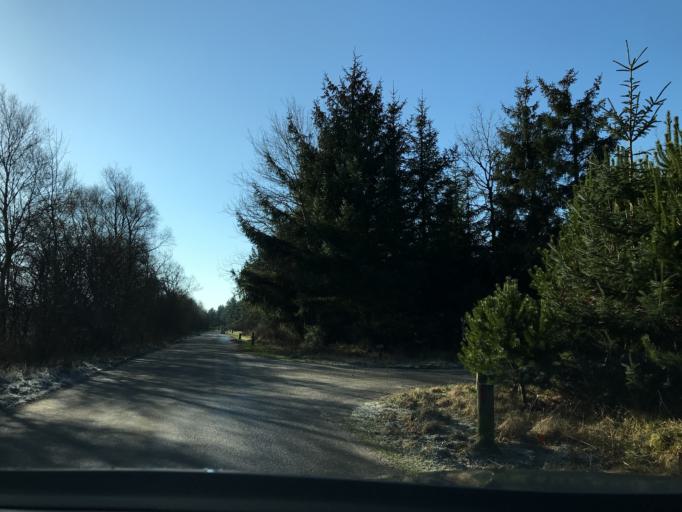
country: DK
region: South Denmark
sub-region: Varde Kommune
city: Oksbol
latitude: 55.7806
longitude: 8.2417
